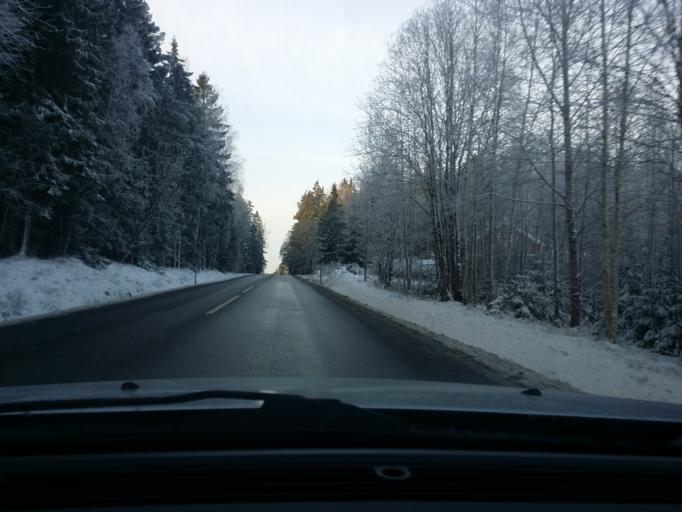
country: SE
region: OErebro
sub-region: Lindesbergs Kommun
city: Frovi
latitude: 59.5171
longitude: 15.3345
